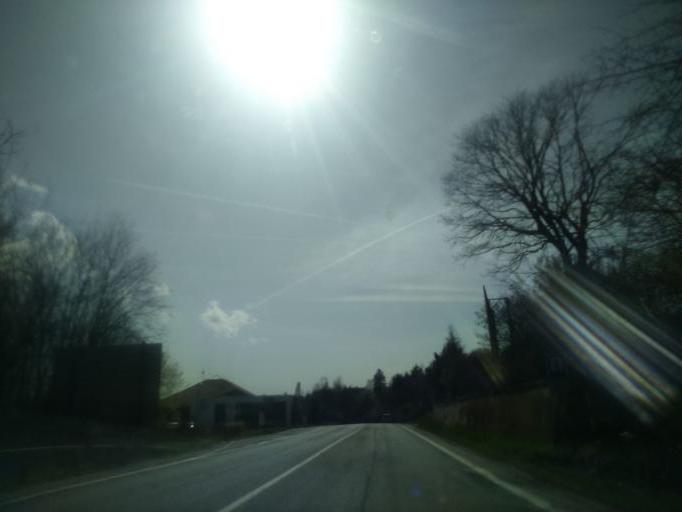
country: CZ
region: Plzensky
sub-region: Okres Tachov
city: Stribro
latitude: 49.7514
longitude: 12.9948
